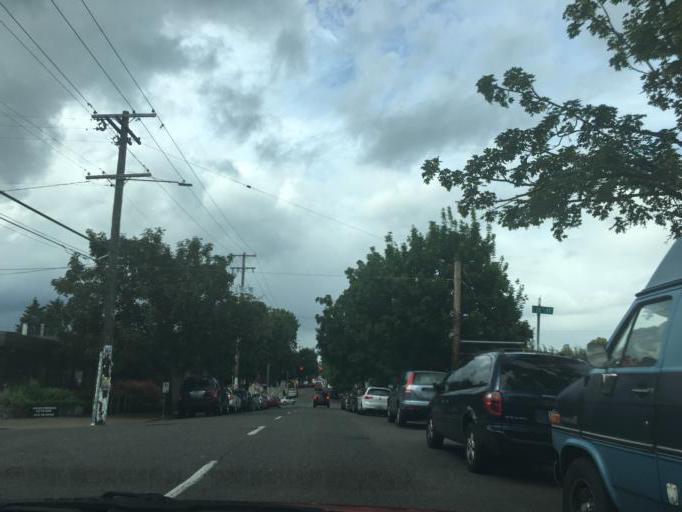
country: US
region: Oregon
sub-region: Multnomah County
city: Portland
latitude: 45.5185
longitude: -122.6536
